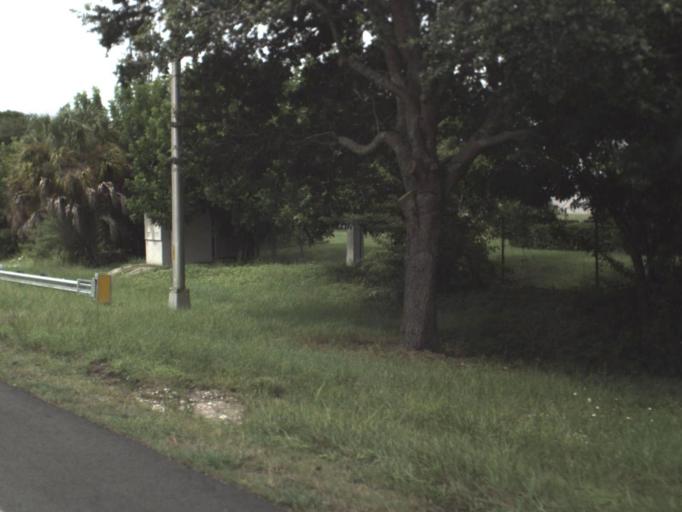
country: US
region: Florida
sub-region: Sarasota County
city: Lake Sarasota
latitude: 27.2989
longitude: -82.4439
